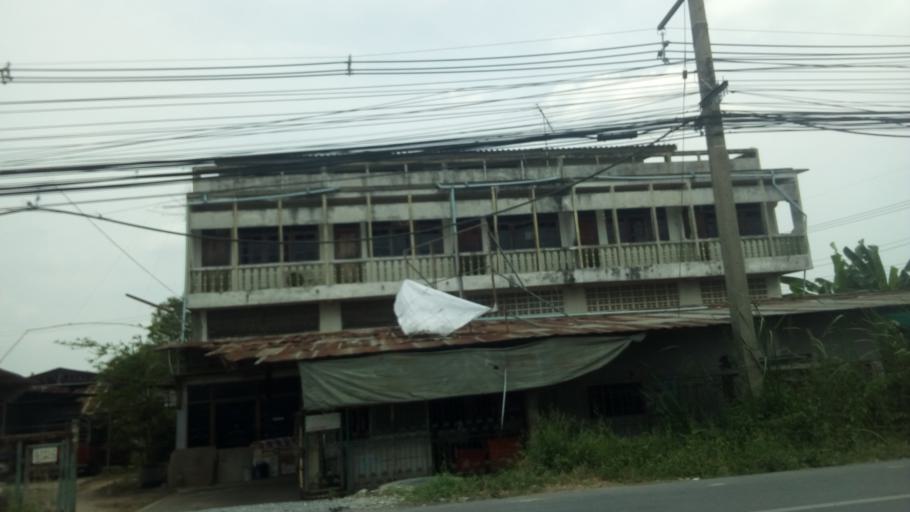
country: TH
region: Nakhon Pathom
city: Salaya
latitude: 13.7790
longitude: 100.3024
